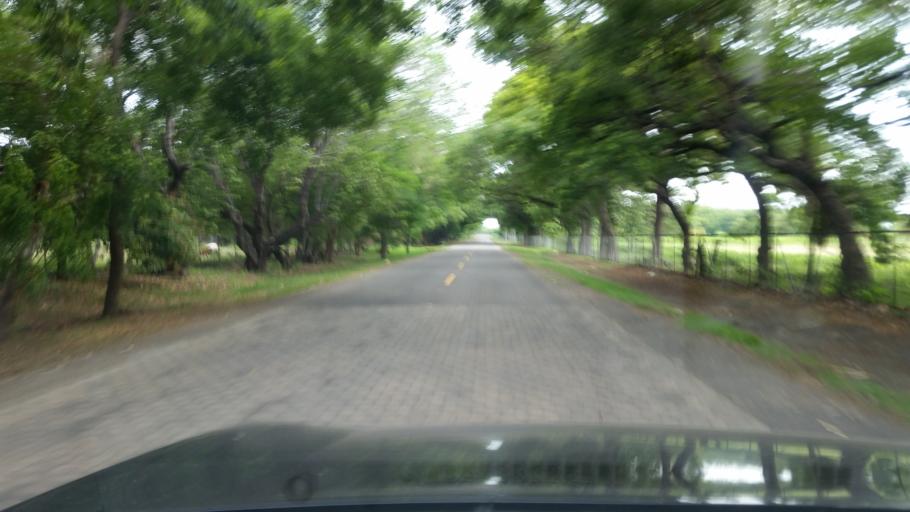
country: NI
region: Managua
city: Carlos Fonseca Amador
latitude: 12.0683
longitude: -86.5011
